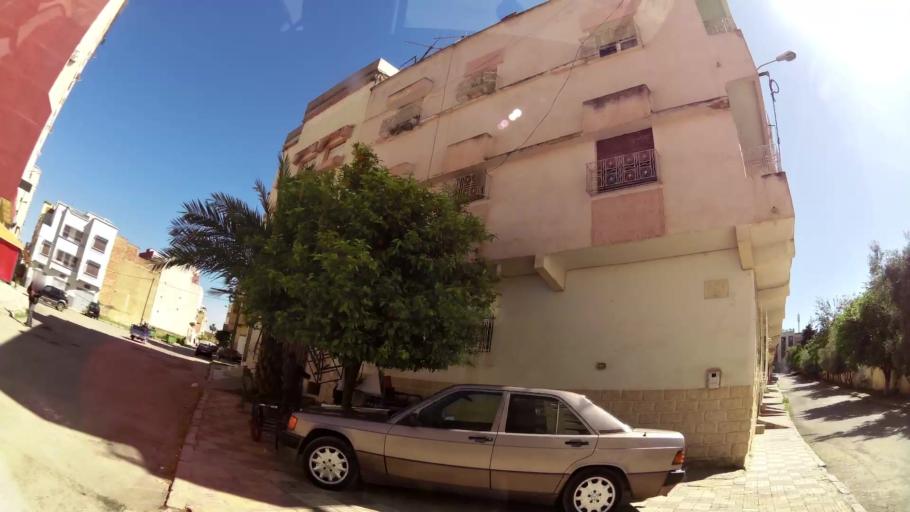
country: MA
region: Meknes-Tafilalet
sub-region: Meknes
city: Meknes
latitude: 33.8841
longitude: -5.5731
